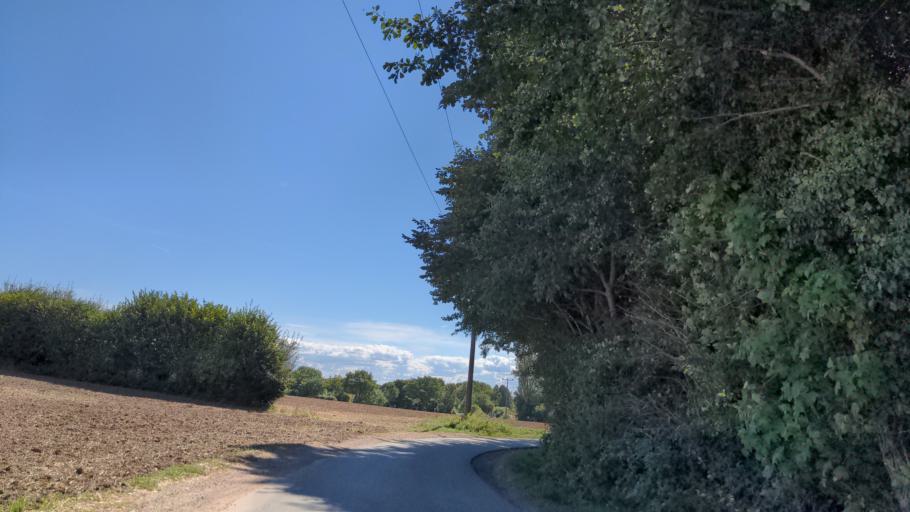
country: DE
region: Schleswig-Holstein
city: Altenkrempe
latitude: 54.1667
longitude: 10.7994
